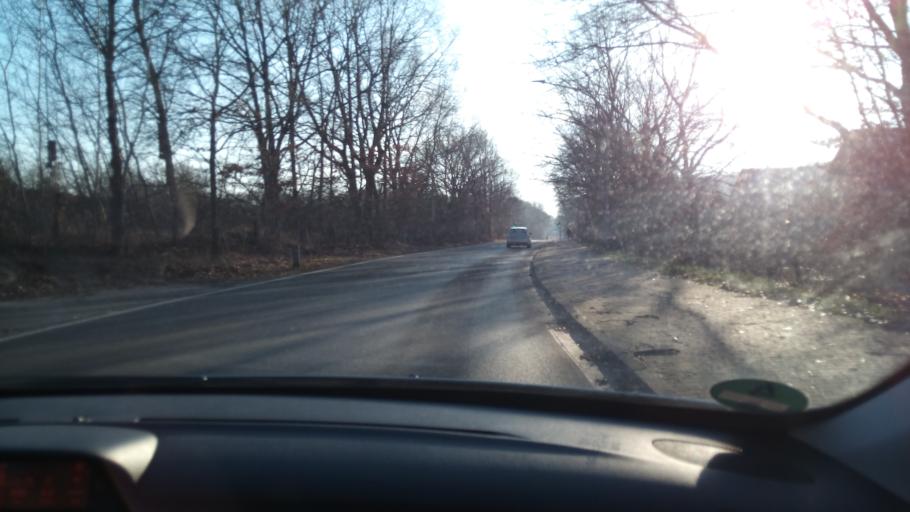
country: DE
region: Schleswig-Holstein
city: Buchen
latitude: 53.4724
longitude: 10.6236
